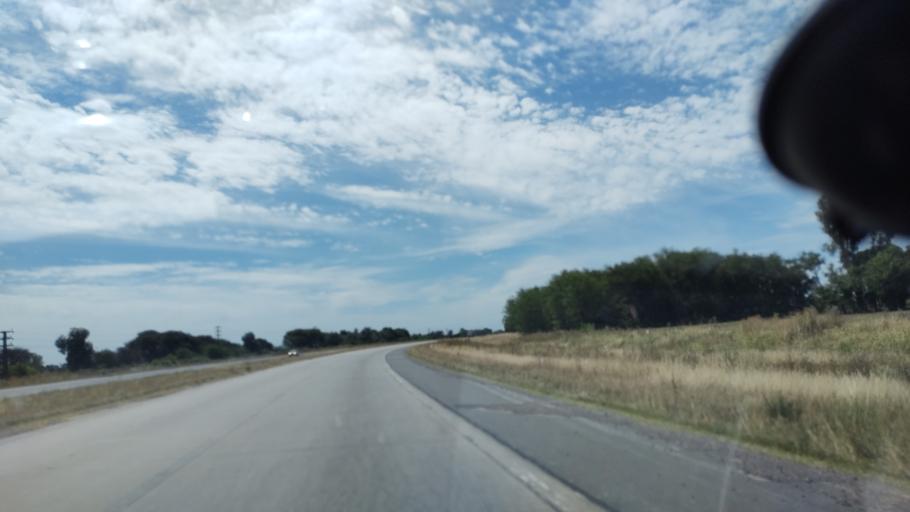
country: AR
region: Buenos Aires
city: Canuelas
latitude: -35.0571
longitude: -58.7077
